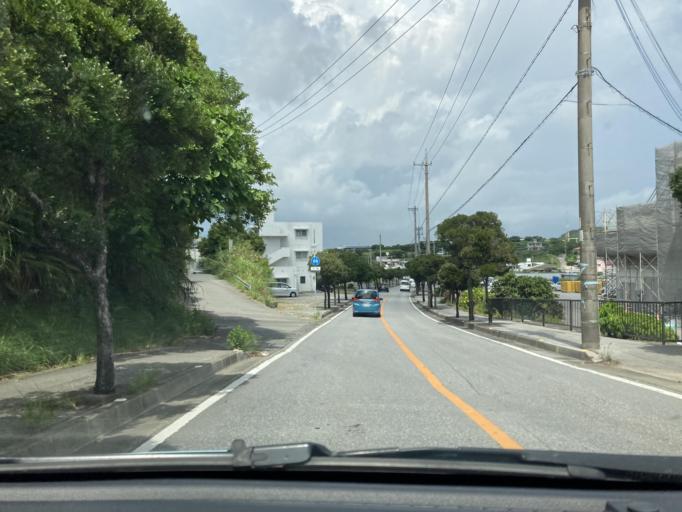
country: JP
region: Okinawa
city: Tomigusuku
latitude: 26.1672
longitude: 127.7544
